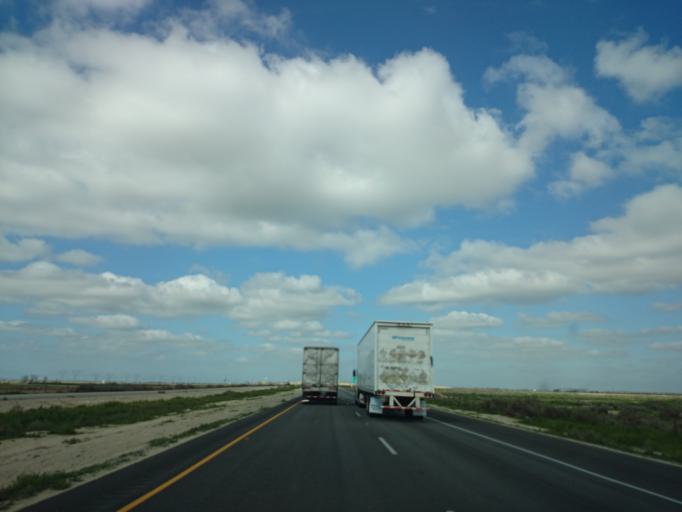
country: US
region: California
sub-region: Kern County
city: Rosedale
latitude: 35.2570
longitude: -119.2135
